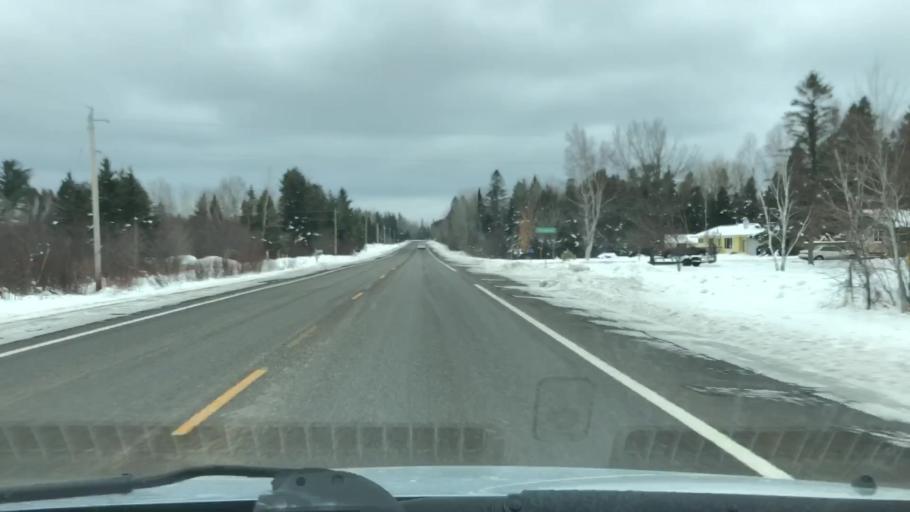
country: US
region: Minnesota
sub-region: Carlton County
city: Esko
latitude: 46.6904
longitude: -92.3648
